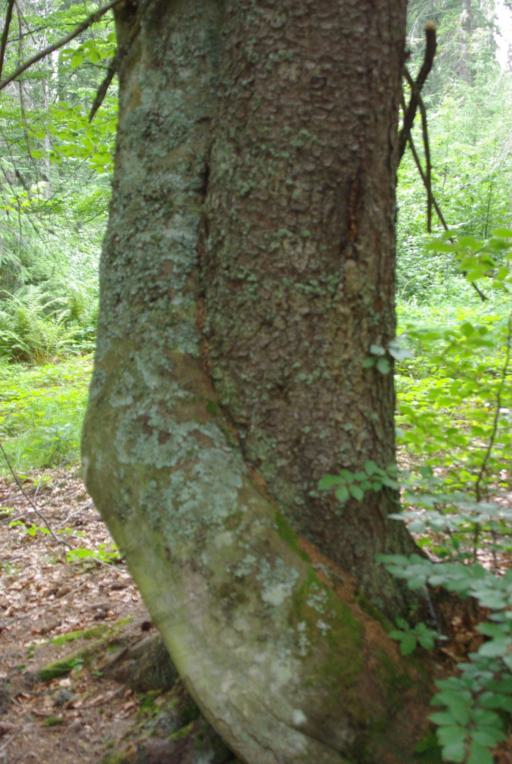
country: RO
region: Alba
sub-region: Comuna Arieseni
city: Arieseni
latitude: 46.5840
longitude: 22.6852
